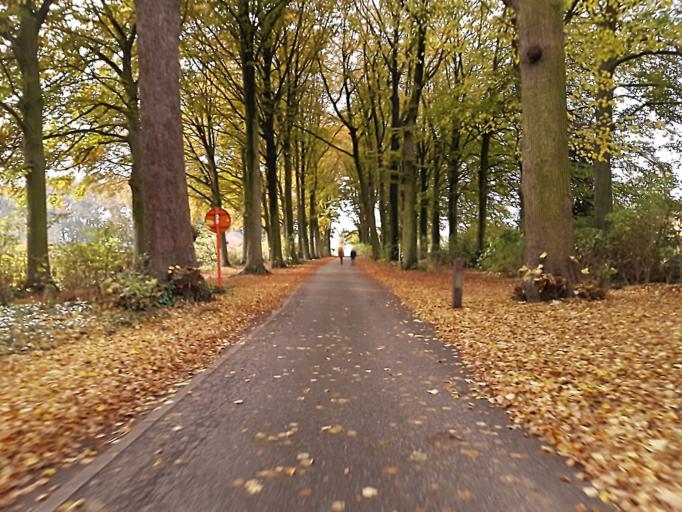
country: BE
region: Flanders
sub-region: Provincie Antwerpen
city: Boechout
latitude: 51.1557
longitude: 4.4925
